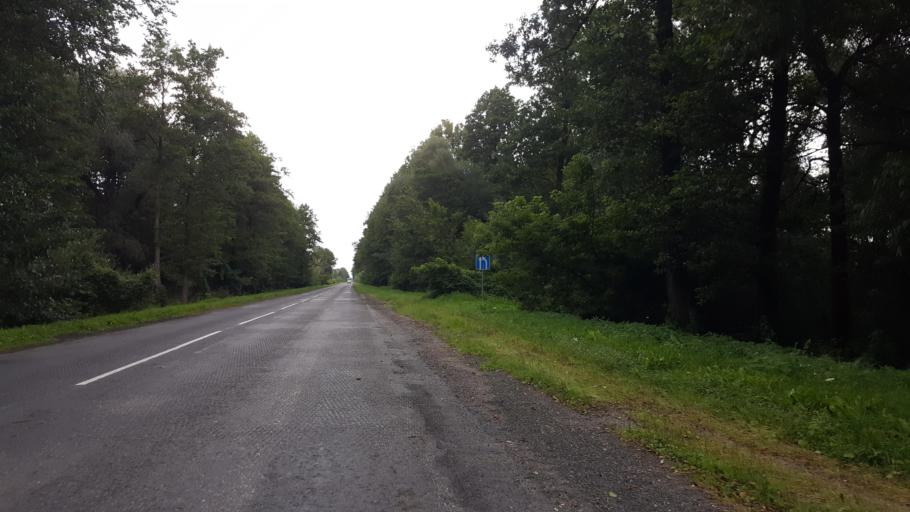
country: BY
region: Brest
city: Zhabinka
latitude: 52.2679
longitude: 23.9575
